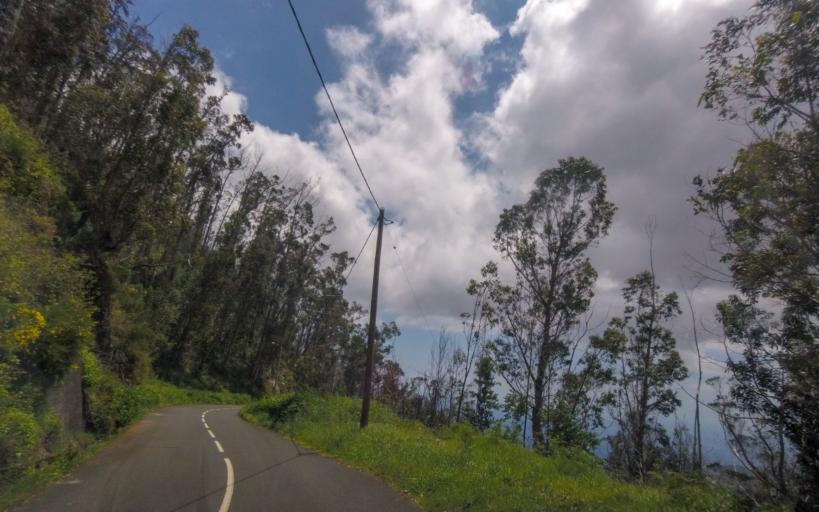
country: PT
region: Madeira
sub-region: Funchal
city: Nossa Senhora do Monte
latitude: 32.6845
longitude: -16.8914
